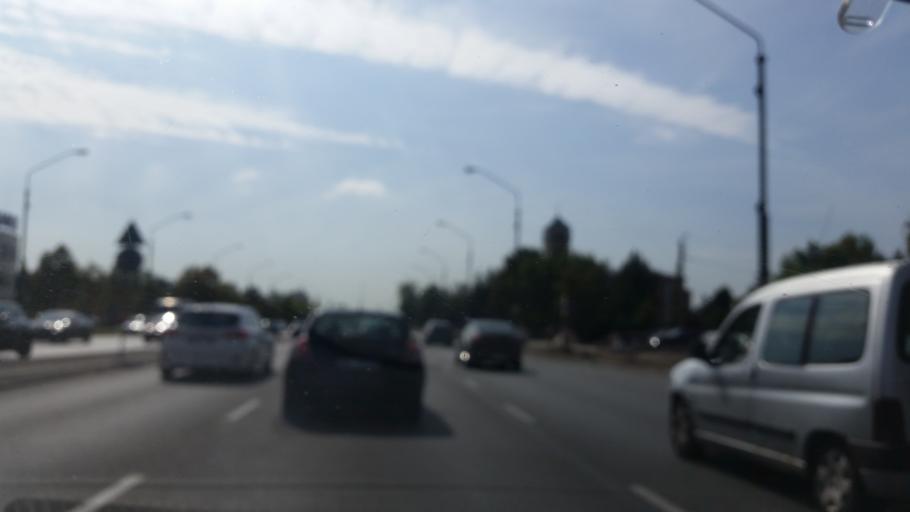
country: PL
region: Masovian Voivodeship
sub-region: Powiat piaseczynski
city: Mysiadlo
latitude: 52.1270
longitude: 21.0180
